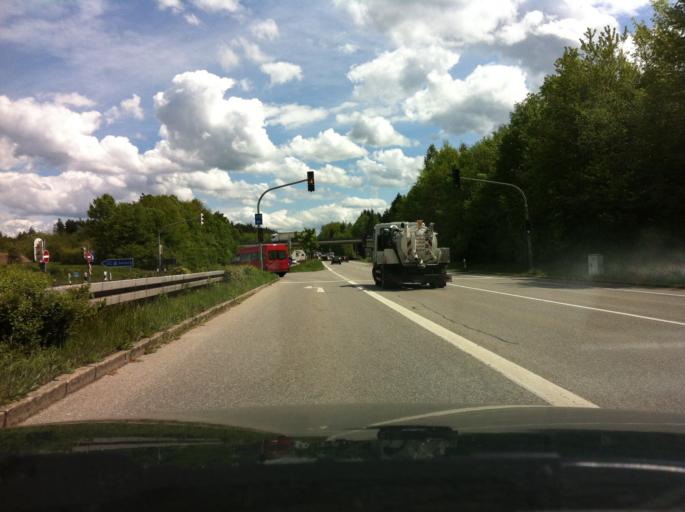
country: DE
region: Bavaria
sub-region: Upper Bavaria
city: Hohenbrunn
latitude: 48.0414
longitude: 11.6781
